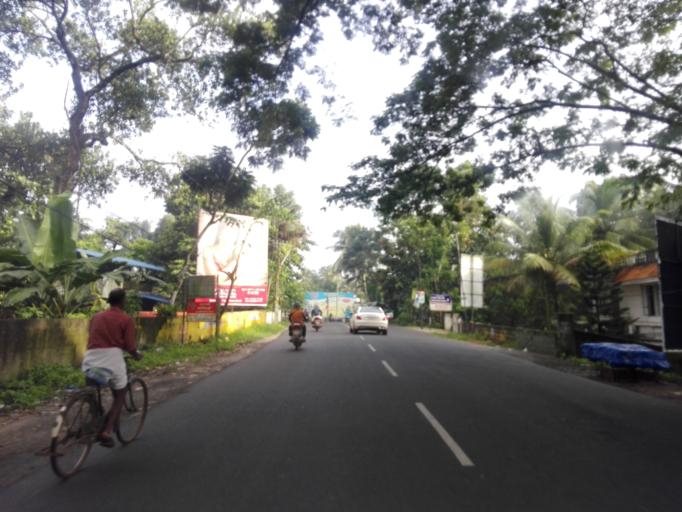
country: IN
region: Kerala
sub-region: Alappuzha
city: Arukutti
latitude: 9.9209
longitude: 76.3617
